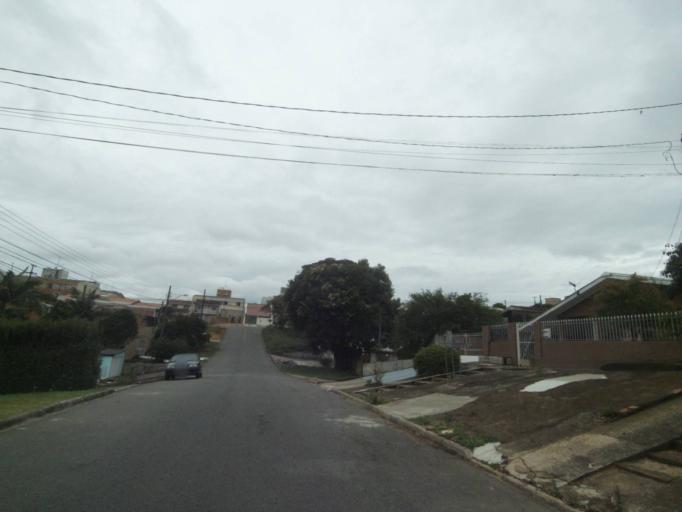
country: BR
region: Parana
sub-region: Curitiba
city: Curitiba
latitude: -25.4566
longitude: -49.3236
